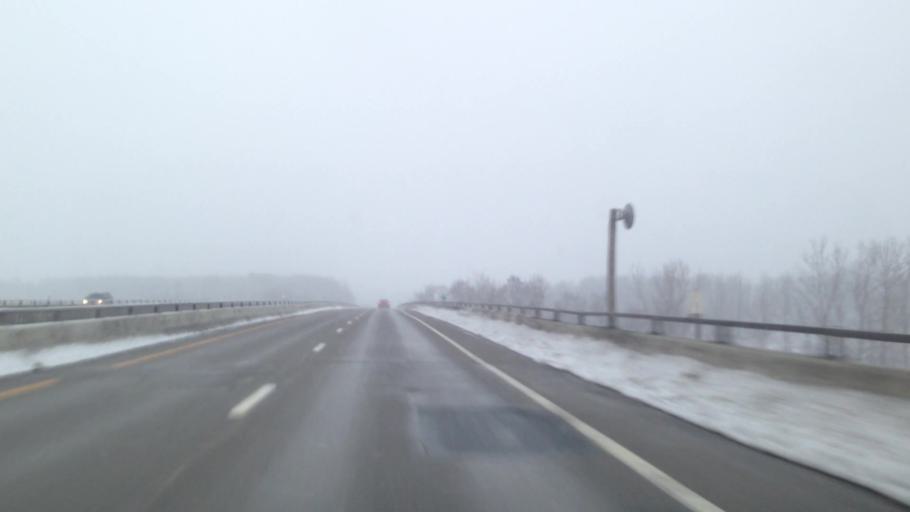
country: US
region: New York
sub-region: Onondaga County
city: East Syracuse
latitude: 43.0673
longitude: -76.0526
